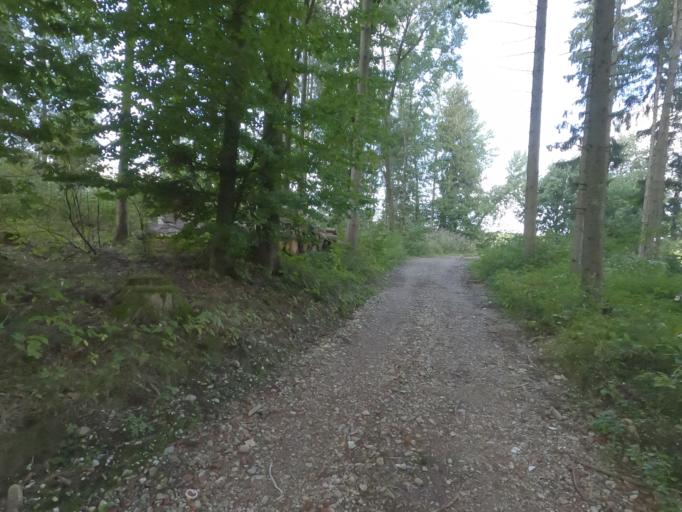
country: DE
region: Bavaria
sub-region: Lower Bavaria
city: Niederalteich
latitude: 48.8121
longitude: 13.0271
